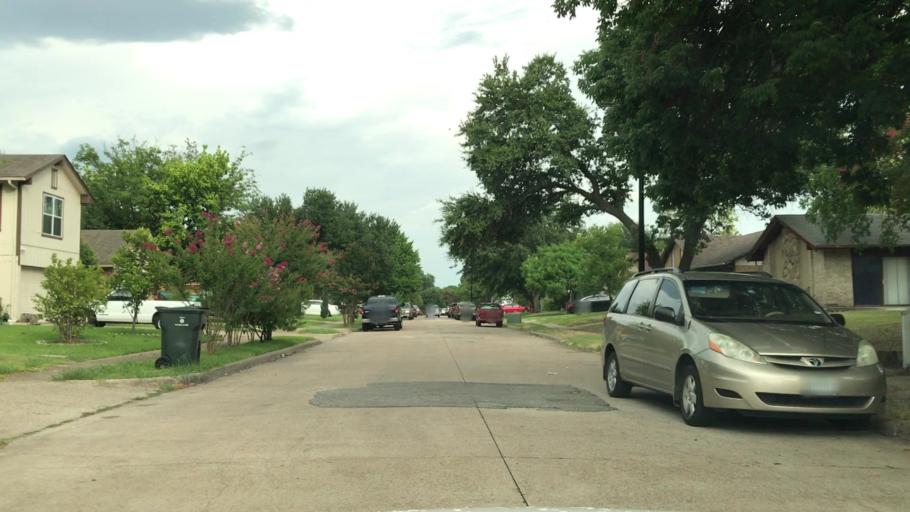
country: US
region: Texas
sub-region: Dallas County
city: Garland
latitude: 32.8623
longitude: -96.6382
